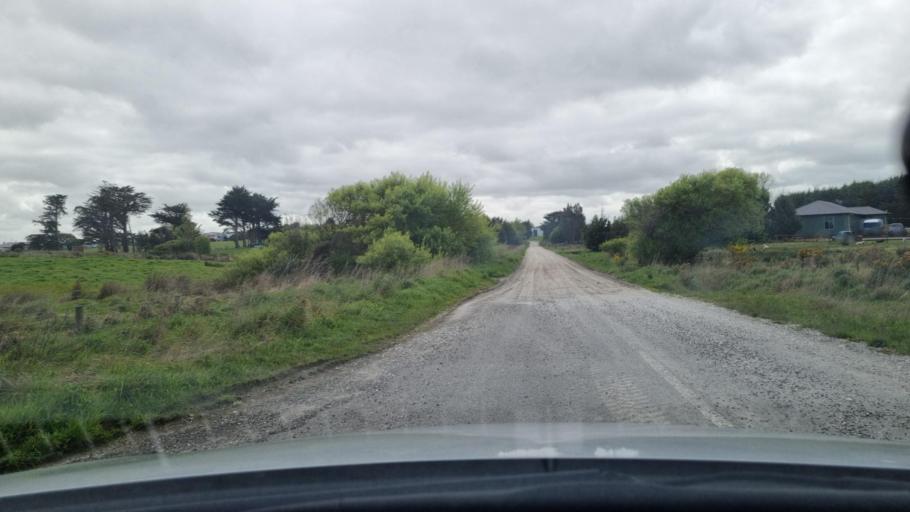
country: NZ
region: Southland
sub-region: Invercargill City
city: Invercargill
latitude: -46.4358
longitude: 168.3896
